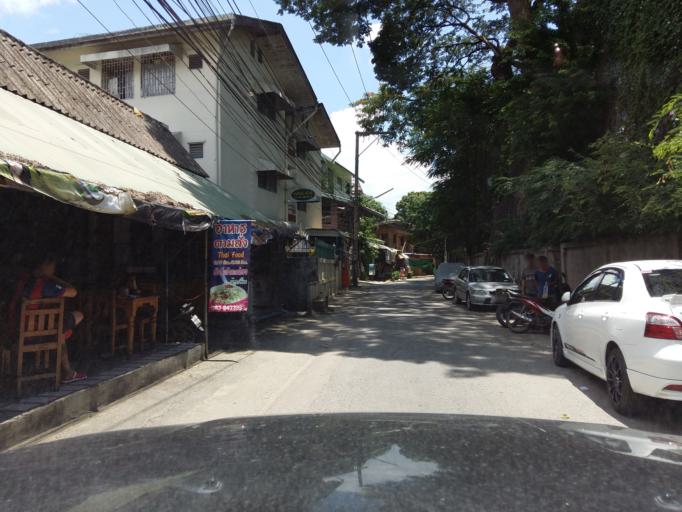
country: TH
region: Chiang Mai
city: Chiang Mai
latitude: 18.7710
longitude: 99.0116
